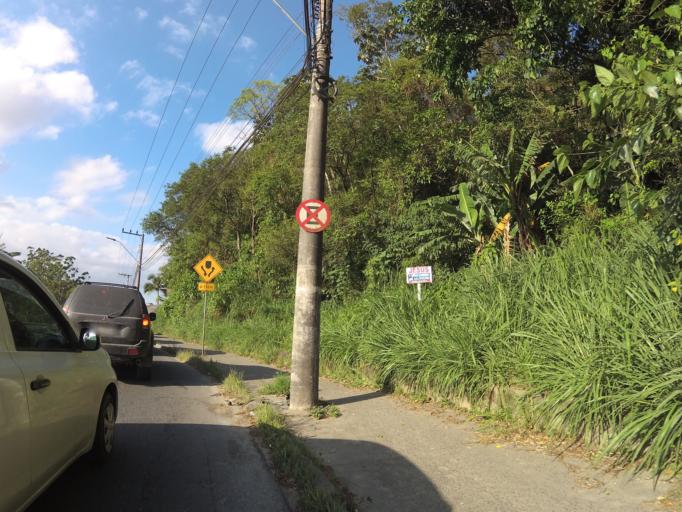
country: BR
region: Santa Catarina
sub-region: Blumenau
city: Blumenau
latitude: -26.9200
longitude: -49.0944
